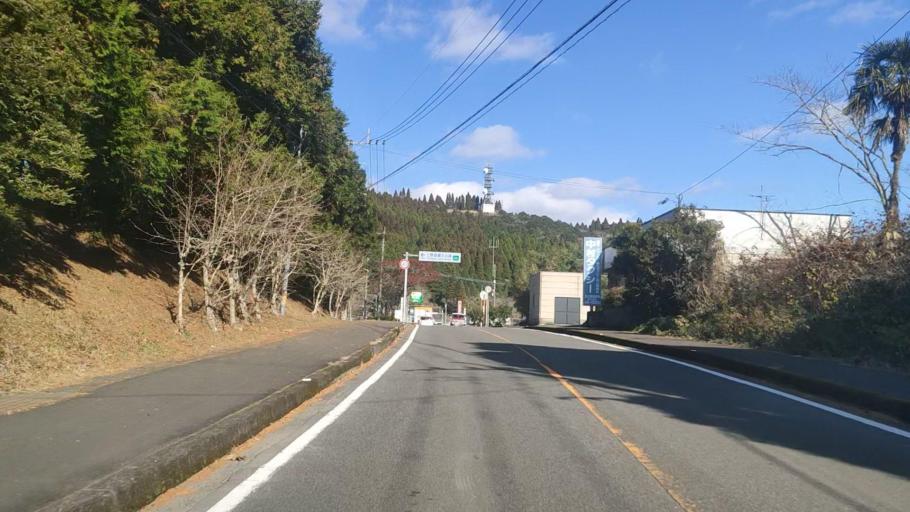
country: JP
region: Kagoshima
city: Kokubu-matsuki
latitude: 31.6706
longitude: 130.8455
